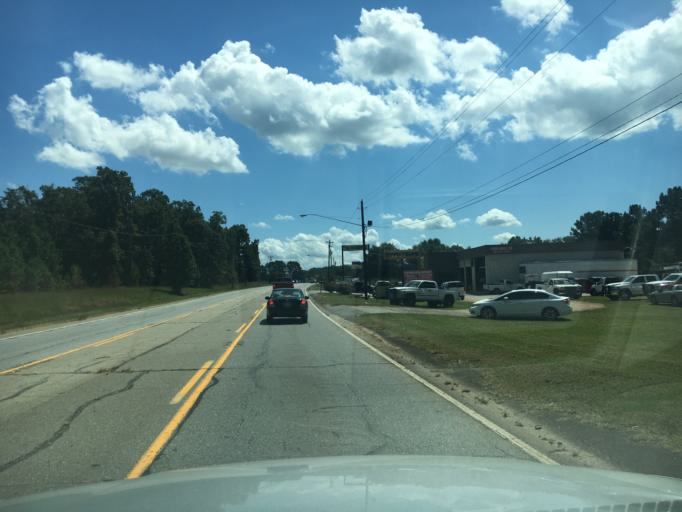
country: US
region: South Carolina
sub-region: Laurens County
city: Laurens
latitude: 34.5008
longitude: -82.0532
